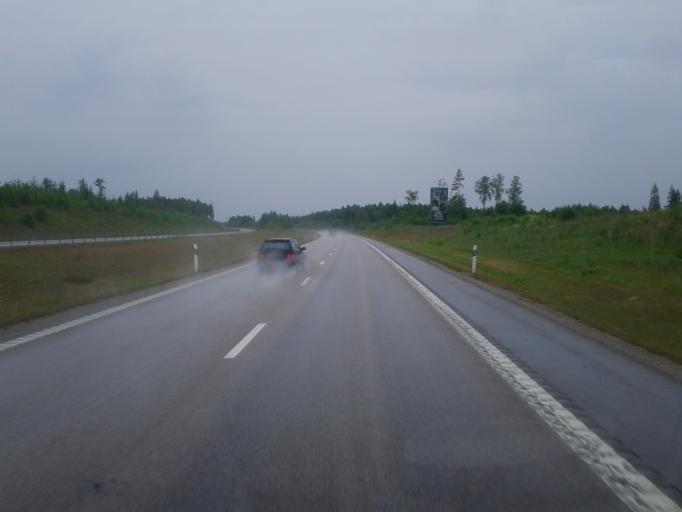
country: SE
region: Uppsala
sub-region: Tierps Kommun
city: Tierp
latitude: 60.3779
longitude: 17.4820
